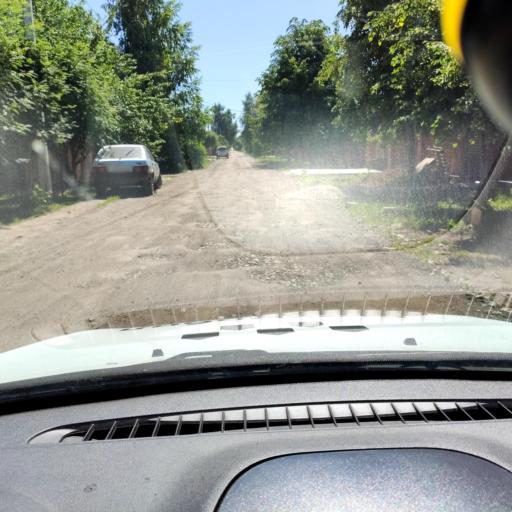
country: RU
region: Samara
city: Tol'yatti
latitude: 53.5658
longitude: 49.3861
